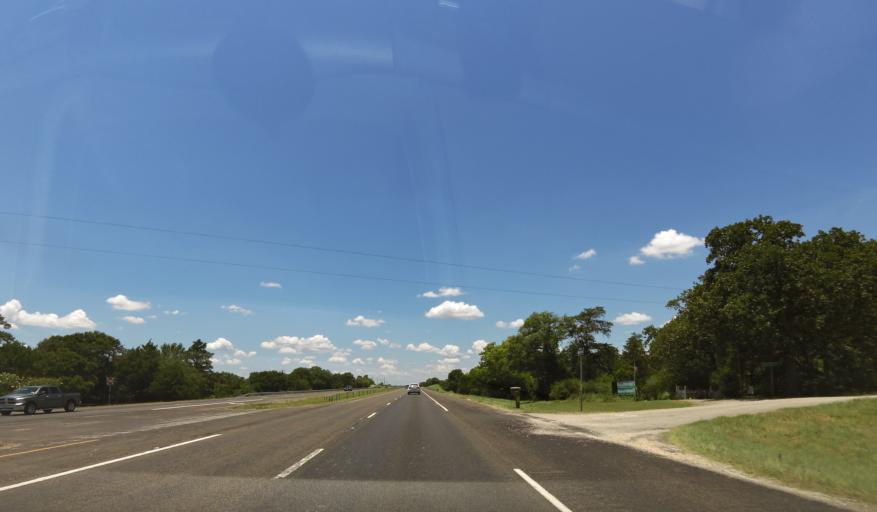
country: US
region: Texas
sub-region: Washington County
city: Brenham
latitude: 30.1847
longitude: -96.4886
